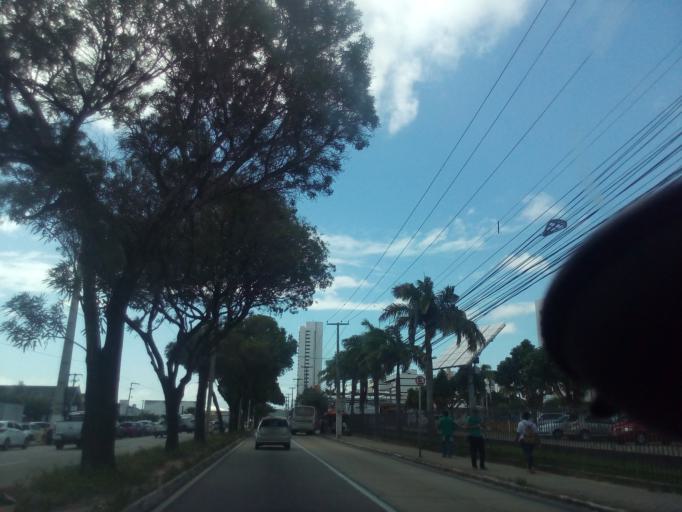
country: BR
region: Rio Grande do Norte
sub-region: Natal
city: Natal
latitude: -5.8240
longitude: -35.2257
